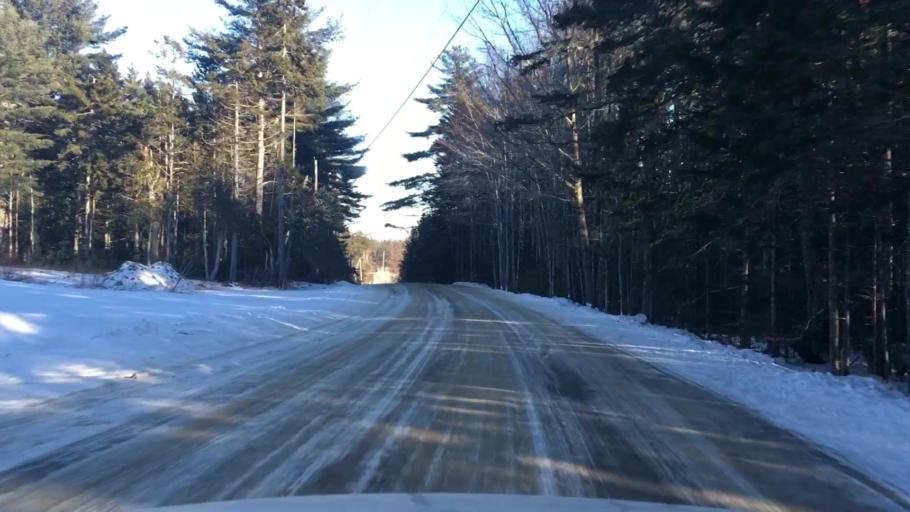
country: US
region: Maine
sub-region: Hancock County
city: Castine
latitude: 44.3824
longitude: -68.7307
